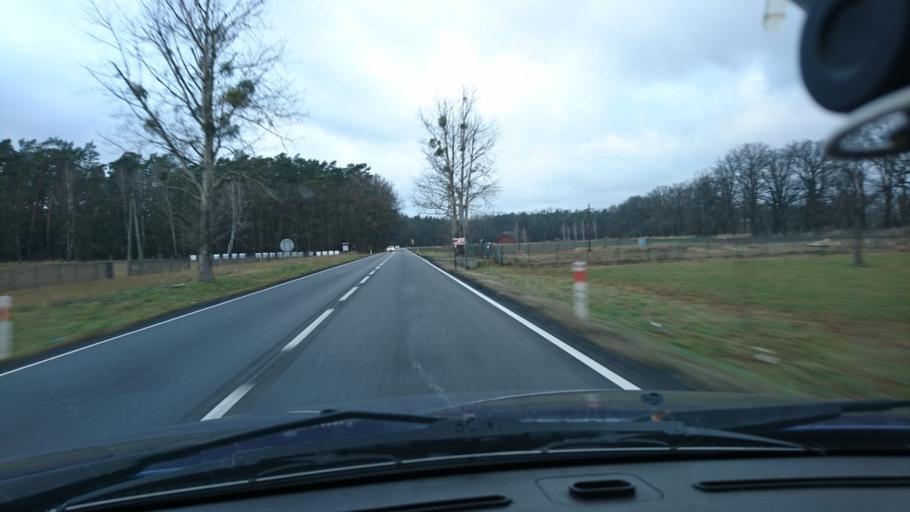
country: PL
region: Opole Voivodeship
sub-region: Powiat oleski
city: Olesno
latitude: 50.9184
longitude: 18.3434
